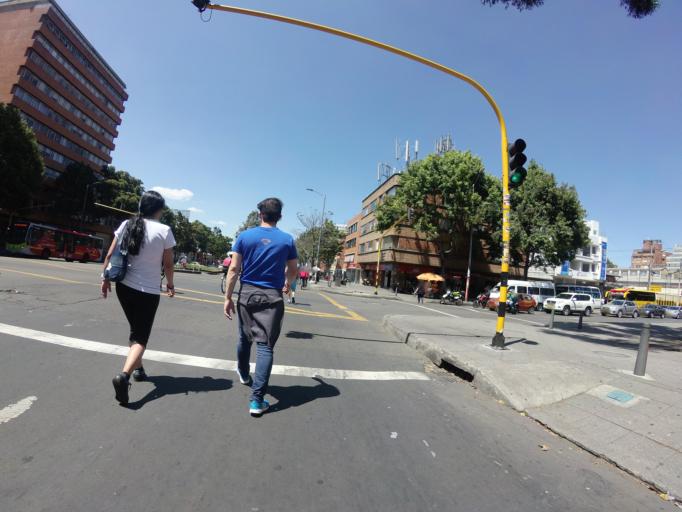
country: CO
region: Bogota D.C.
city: Barrio San Luis
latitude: 4.6584
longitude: -74.0602
